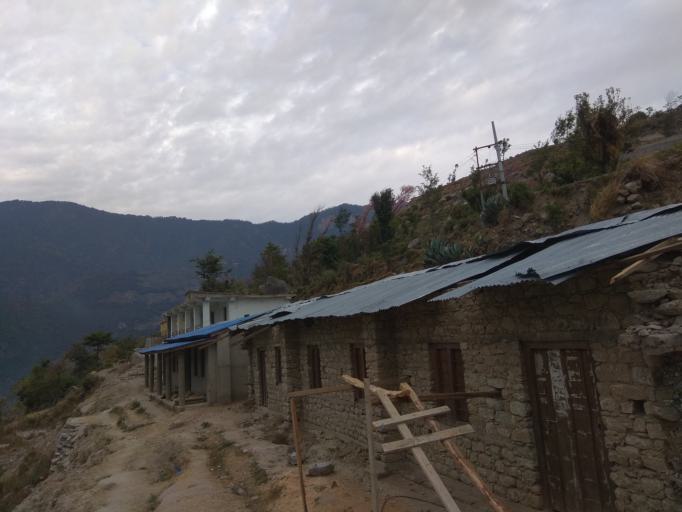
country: NP
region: Far Western
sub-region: Seti Zone
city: Achham
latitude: 29.2340
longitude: 81.6395
